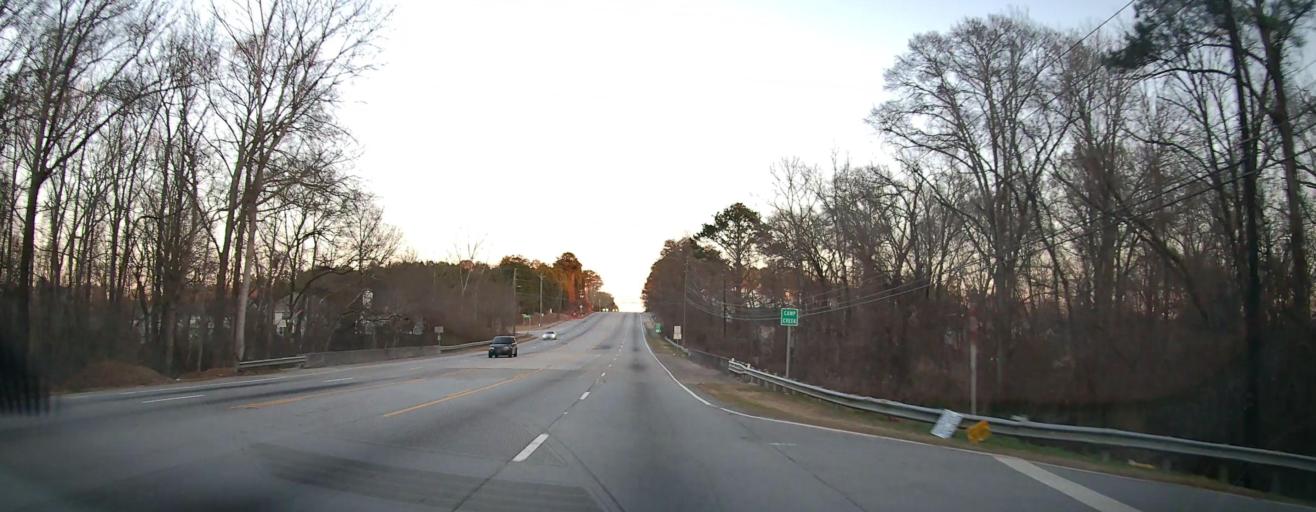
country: US
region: Georgia
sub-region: Clayton County
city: Riverdale
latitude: 33.5507
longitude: -84.4403
